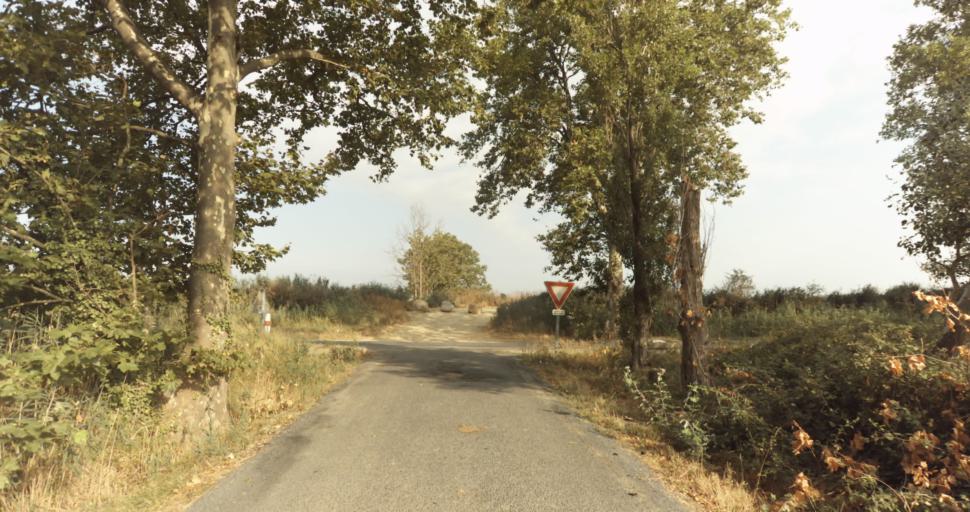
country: FR
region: Languedoc-Roussillon
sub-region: Departement des Pyrenees-Orientales
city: Montescot
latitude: 42.6165
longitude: 2.9392
